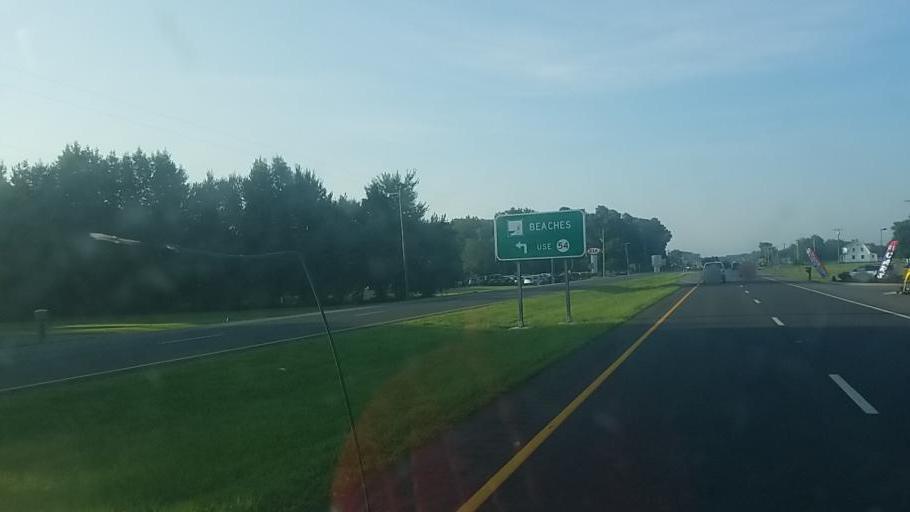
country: US
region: Delaware
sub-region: Sussex County
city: Selbyville
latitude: 38.4678
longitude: -75.2344
